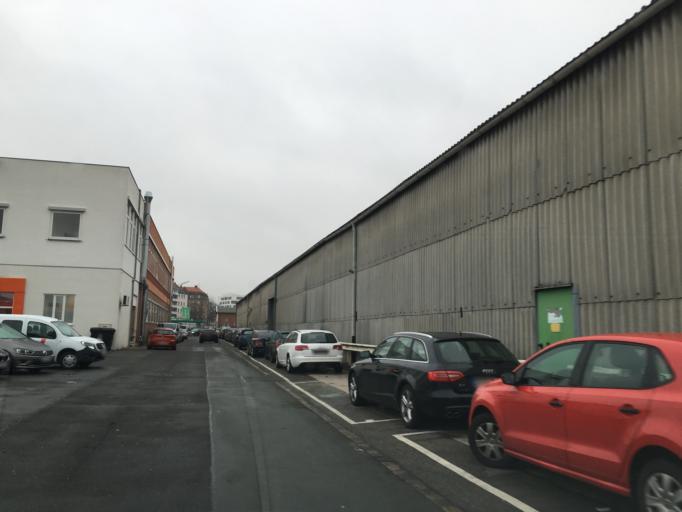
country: DE
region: Bavaria
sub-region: Regierungsbezirk Mittelfranken
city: Nuernberg
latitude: 49.4298
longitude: 11.0812
